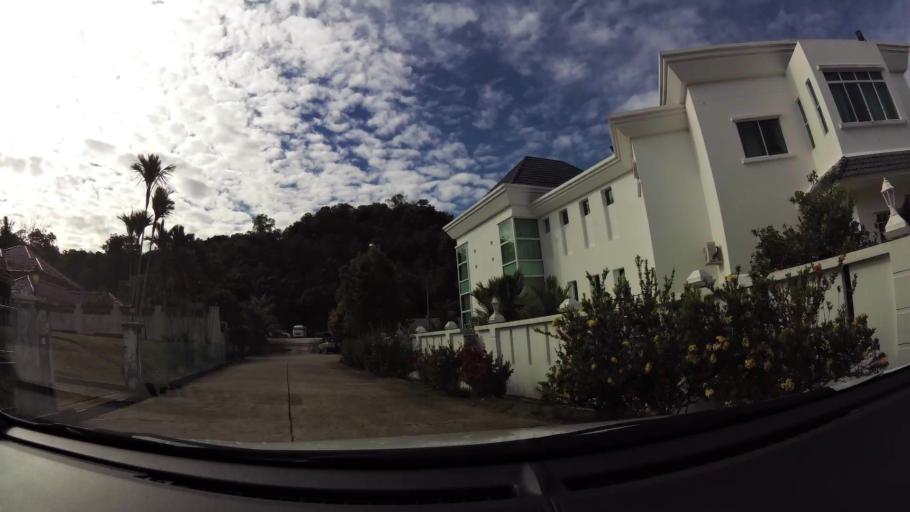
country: BN
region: Brunei and Muara
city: Bandar Seri Begawan
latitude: 4.8938
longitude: 114.9693
